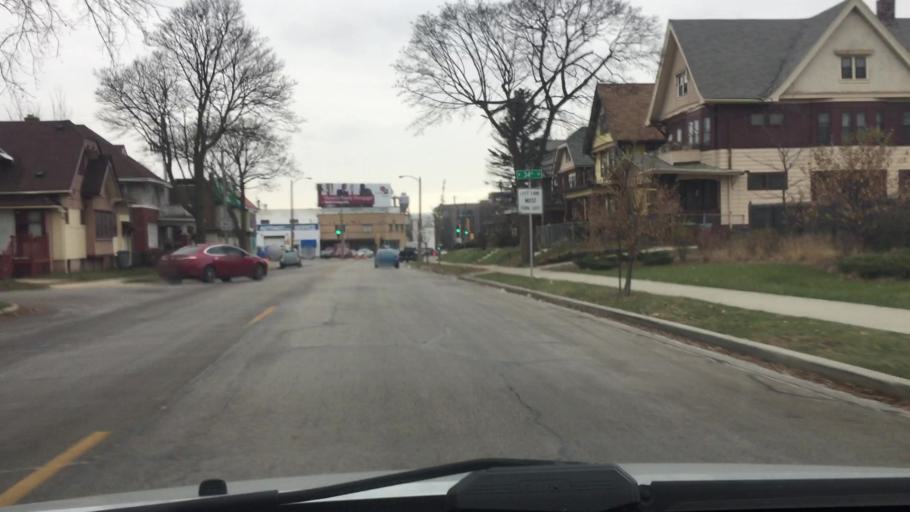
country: US
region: Wisconsin
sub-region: Milwaukee County
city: West Milwaukee
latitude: 43.0433
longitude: -87.9561
